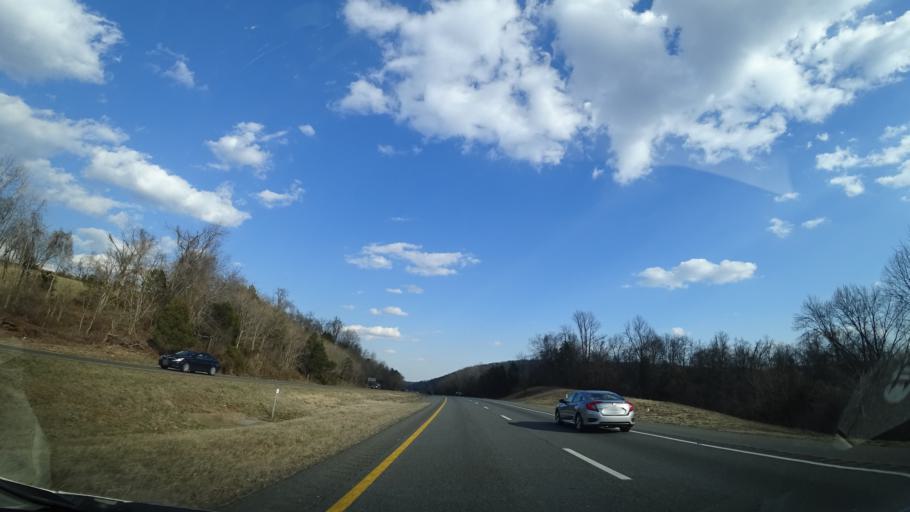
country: US
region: Virginia
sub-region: Fauquier County
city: New Baltimore
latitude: 38.8287
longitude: -77.7314
